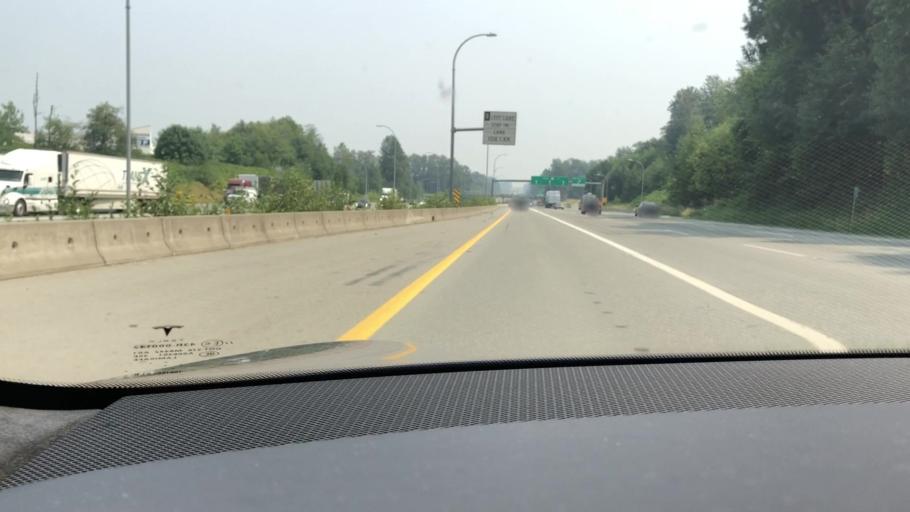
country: CA
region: British Columbia
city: Pitt Meadows
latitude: 49.1724
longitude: -122.7005
